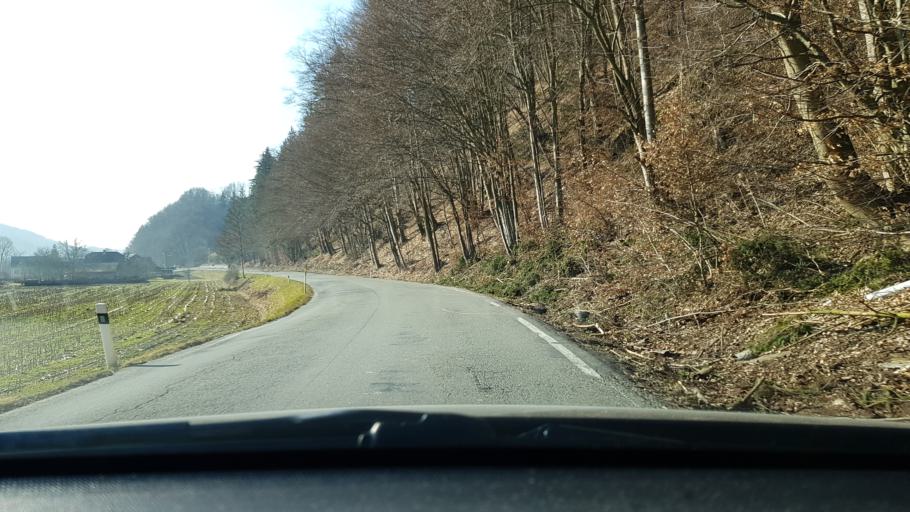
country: CZ
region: Olomoucky
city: Dolni Bohdikov
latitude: 50.0124
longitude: 16.8954
